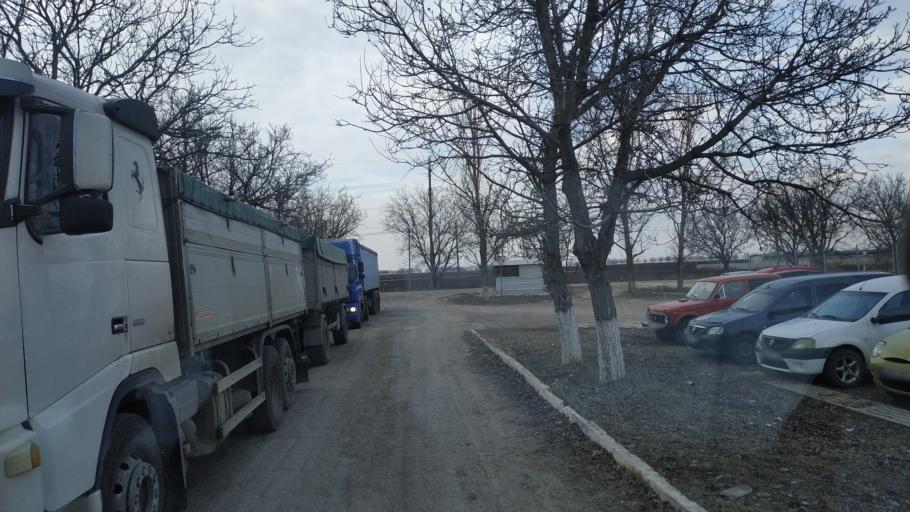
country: MD
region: Anenii Noi
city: Anenii Noi
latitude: 46.9165
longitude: 29.3353
